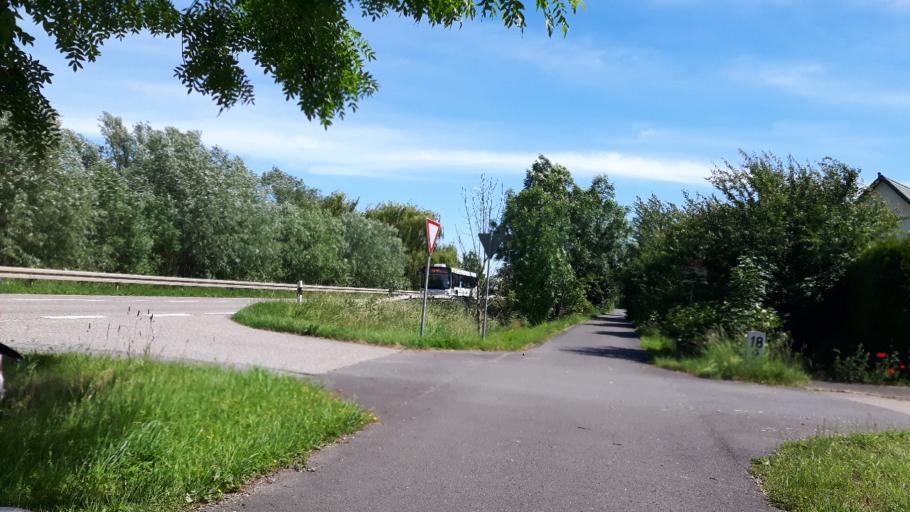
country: DE
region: Saxony-Anhalt
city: Lutzen
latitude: 51.2412
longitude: 12.1186
